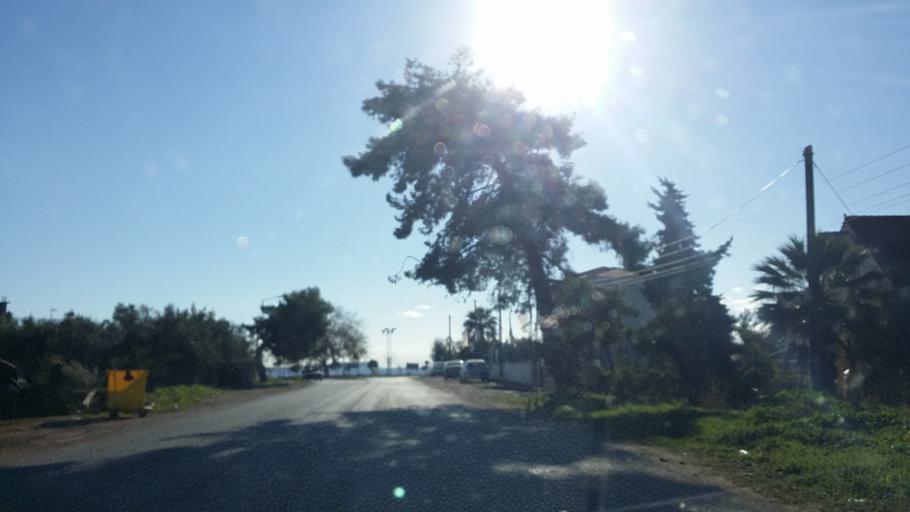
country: GR
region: West Greece
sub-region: Nomos Aitolias kai Akarnanias
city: Astakos
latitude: 38.5363
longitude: 21.0896
